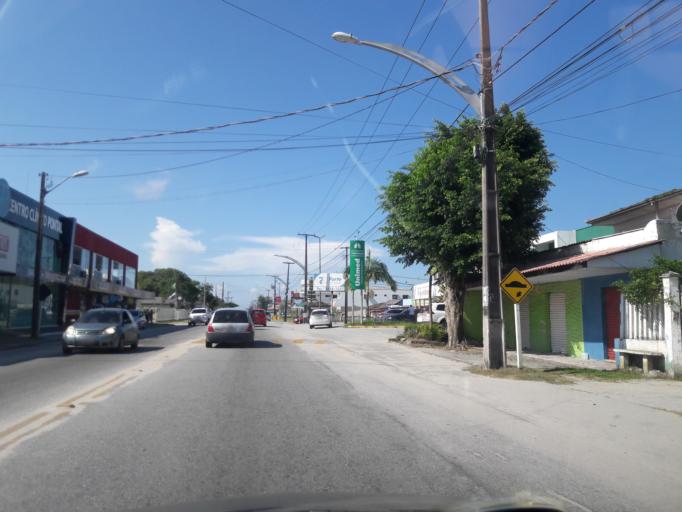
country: BR
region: Parana
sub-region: Pontal Do Parana
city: Pontal do Parana
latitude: -25.6940
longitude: -48.4741
